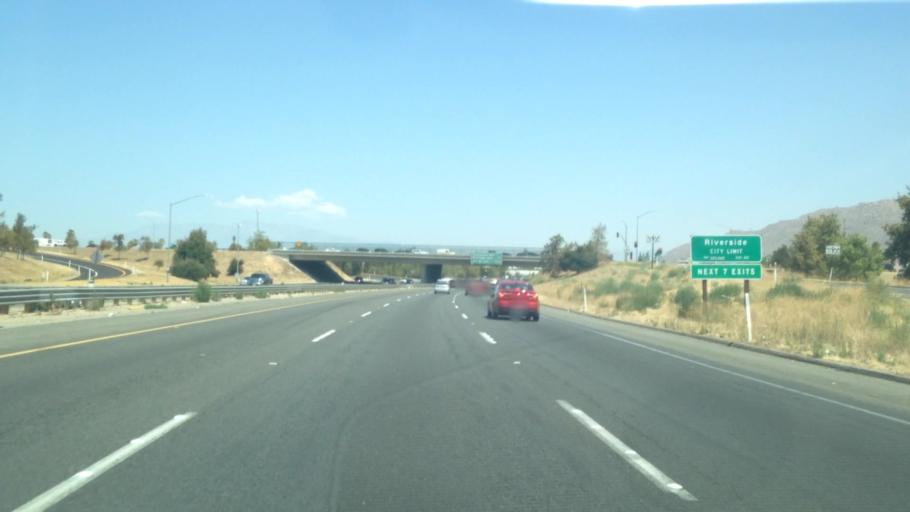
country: US
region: California
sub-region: Riverside County
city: March Air Force Base
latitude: 33.9149
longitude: -117.2864
